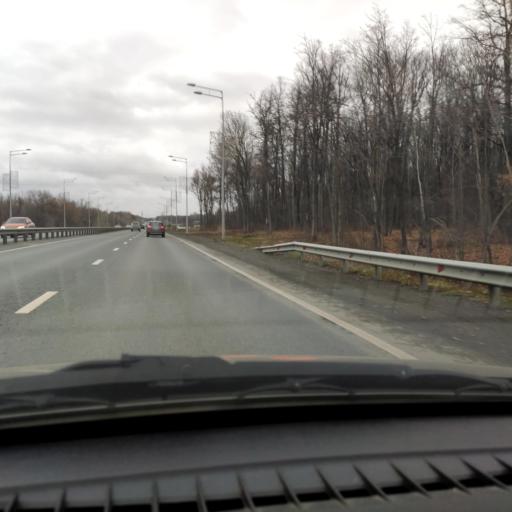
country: RU
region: Samara
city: Novosemeykino
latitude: 53.3342
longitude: 50.2320
